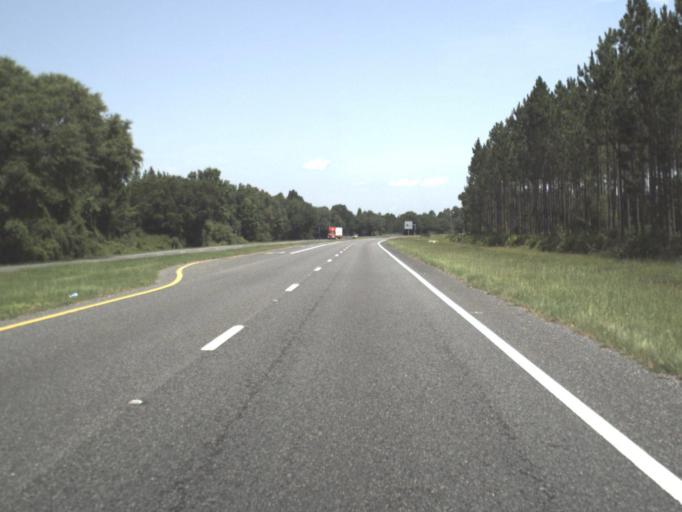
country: US
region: Florida
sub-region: Taylor County
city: Steinhatchee
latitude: 29.7449
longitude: -83.3200
